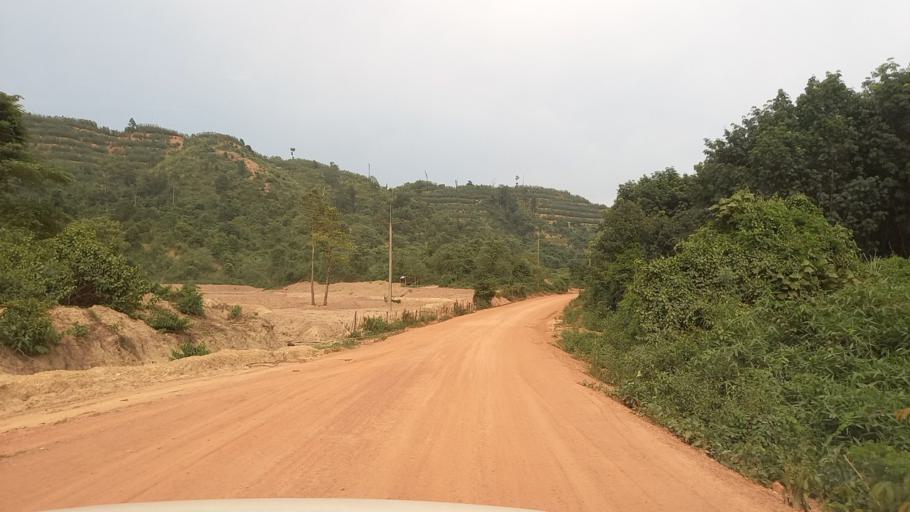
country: LA
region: Bolikhamxai
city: Bolikhan
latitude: 18.5177
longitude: 103.8342
